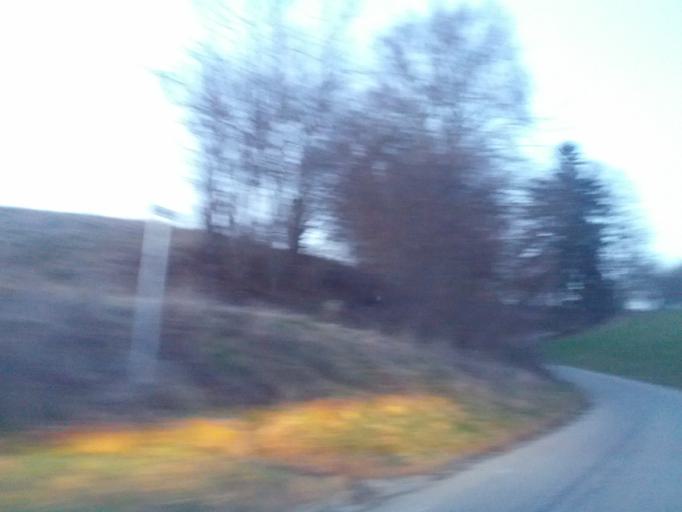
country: DE
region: Baden-Wuerttemberg
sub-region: Tuebingen Region
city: Steinhausen an der Rottum
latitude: 47.9812
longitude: 9.9827
